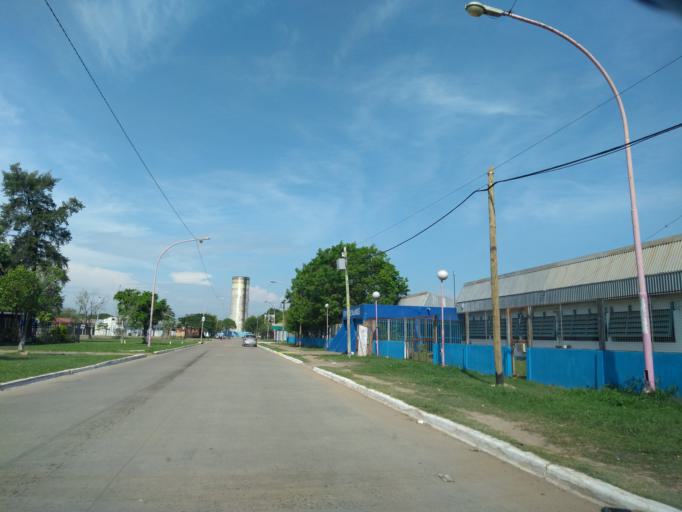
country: AR
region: Chaco
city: Barranqueras
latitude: -27.4619
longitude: -58.9488
